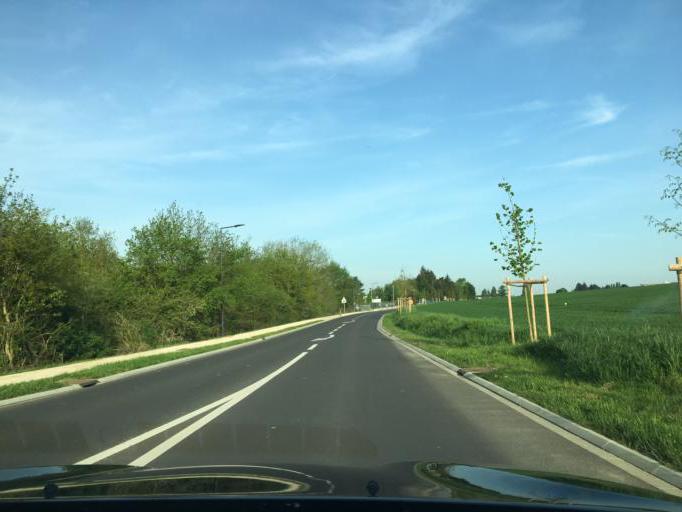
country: FR
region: Centre
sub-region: Departement d'Eure-et-Loir
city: Droue-sur-Drouette
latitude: 48.5968
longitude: 1.6930
